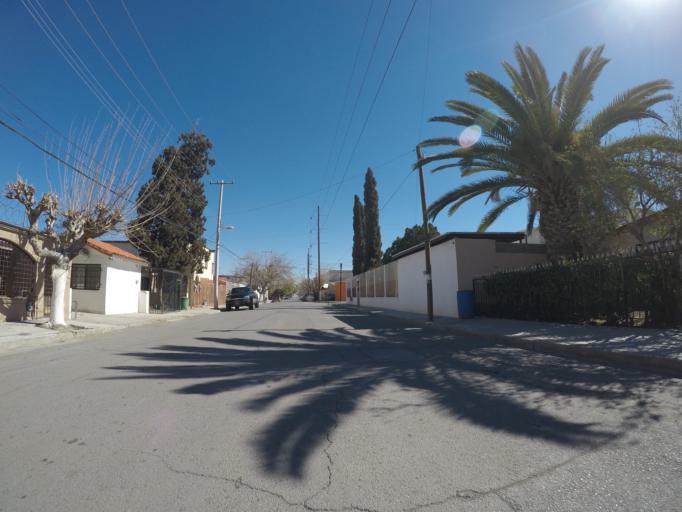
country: MX
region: Chihuahua
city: Ciudad Juarez
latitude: 31.7320
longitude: -106.4388
